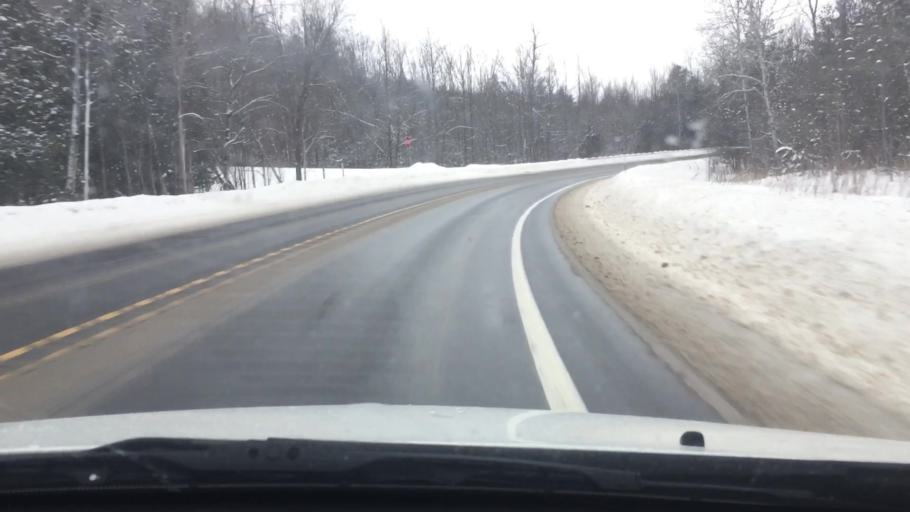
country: US
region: Michigan
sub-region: Charlevoix County
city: East Jordan
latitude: 45.1292
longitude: -85.0799
